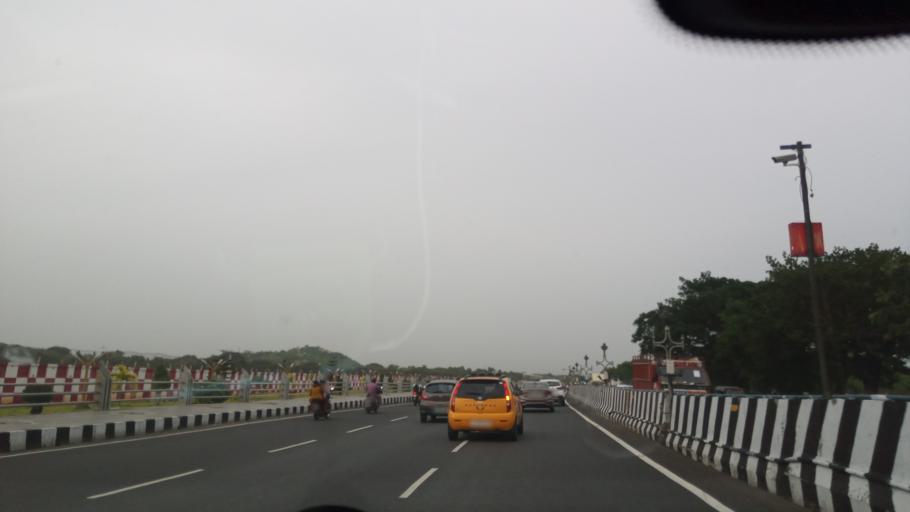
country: IN
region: Tamil Nadu
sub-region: Kancheepuram
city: Saint Thomas Mount
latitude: 12.9924
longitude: 80.1826
